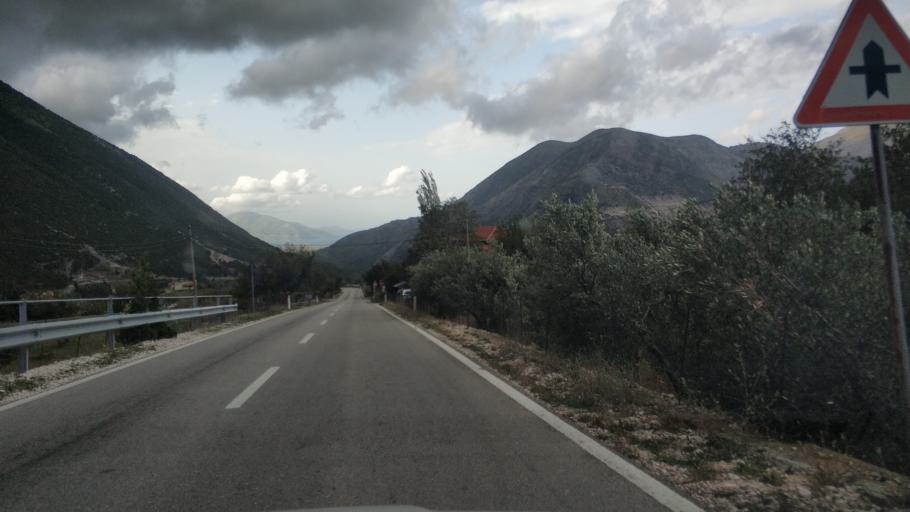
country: AL
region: Vlore
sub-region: Rrethi i Vlores
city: Brataj
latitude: 40.2330
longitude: 19.5622
